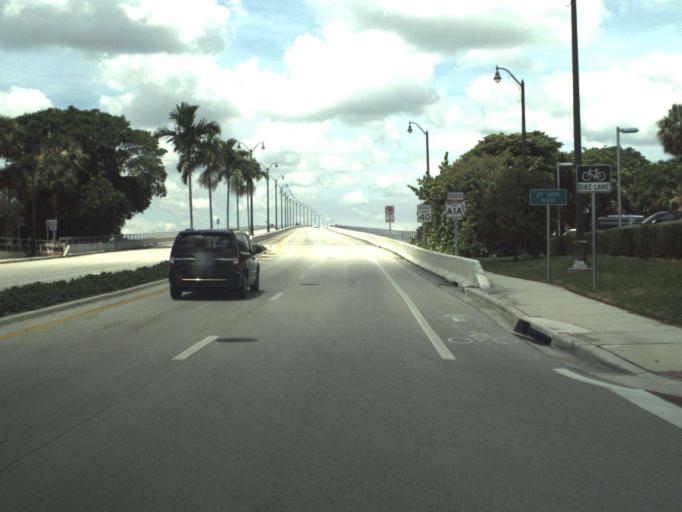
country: US
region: Florida
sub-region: Martin County
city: Sewall's Point
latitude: 27.2019
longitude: -80.2028
